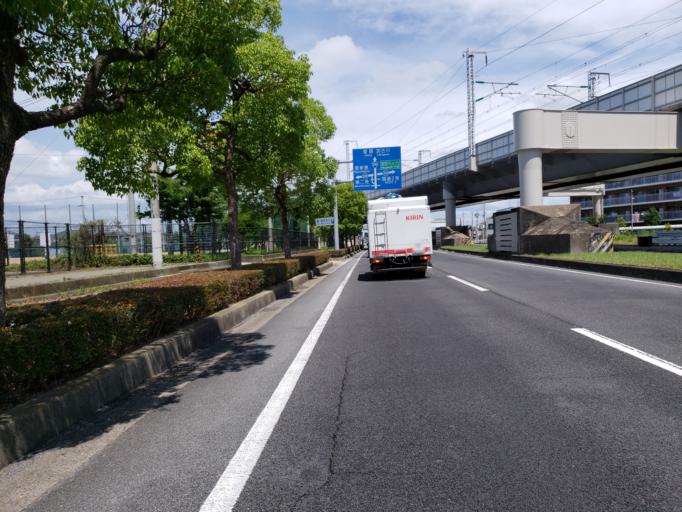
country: JP
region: Hyogo
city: Kakogawacho-honmachi
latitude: 34.7065
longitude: 134.8848
